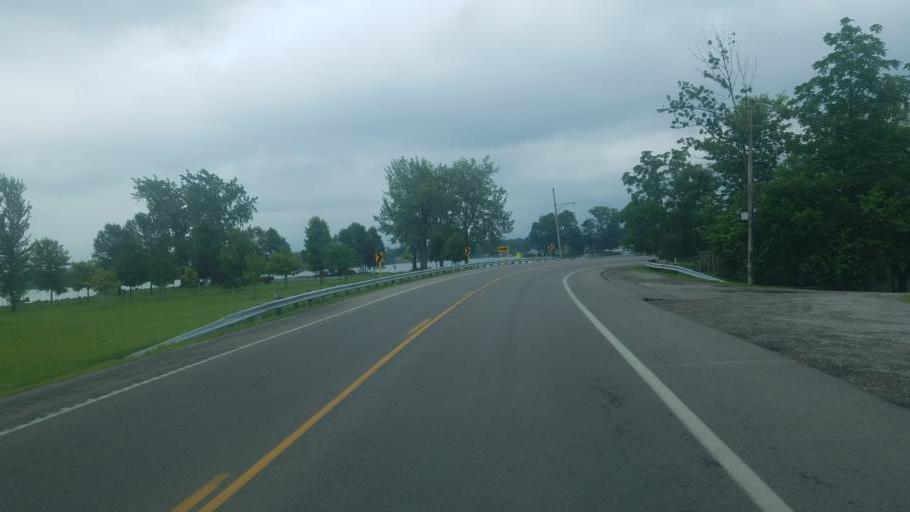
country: US
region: Ohio
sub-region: Logan County
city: Russells Point
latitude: 40.4801
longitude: -83.8997
